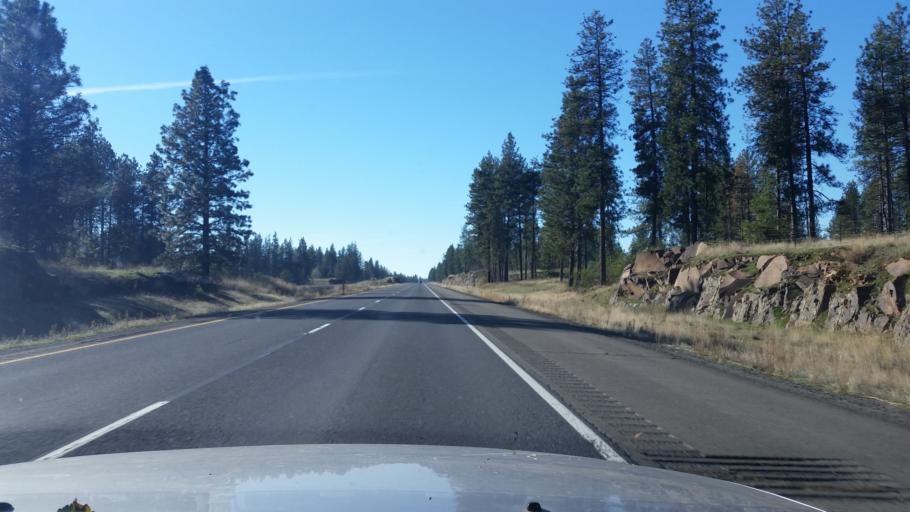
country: US
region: Washington
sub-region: Spokane County
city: Medical Lake
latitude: 47.5234
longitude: -117.6650
